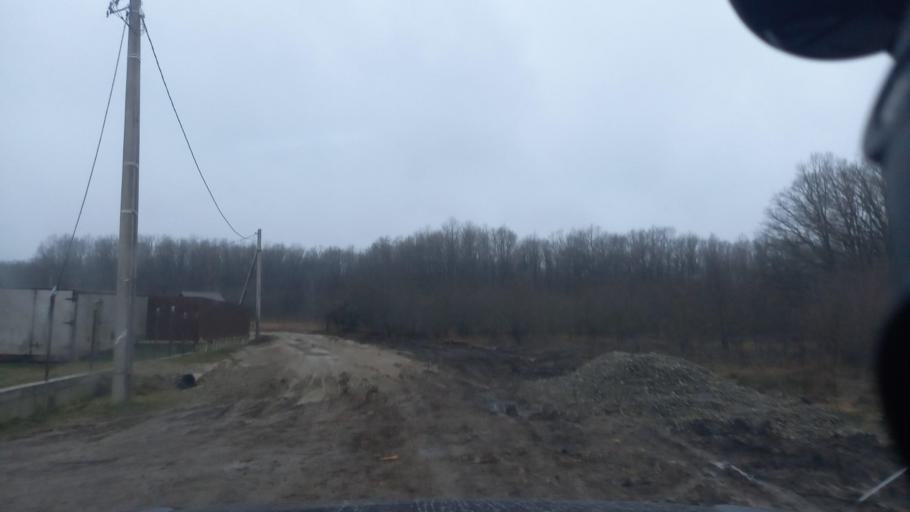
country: RU
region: Krasnodarskiy
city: Saratovskaya
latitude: 44.6467
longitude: 39.3047
